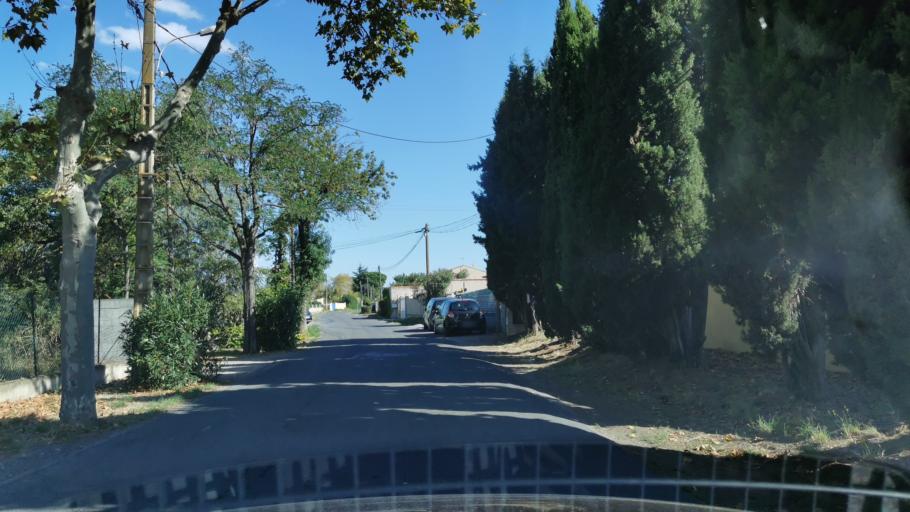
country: FR
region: Languedoc-Roussillon
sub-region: Departement de l'Aude
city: Ginestas
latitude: 43.2466
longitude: 2.8944
